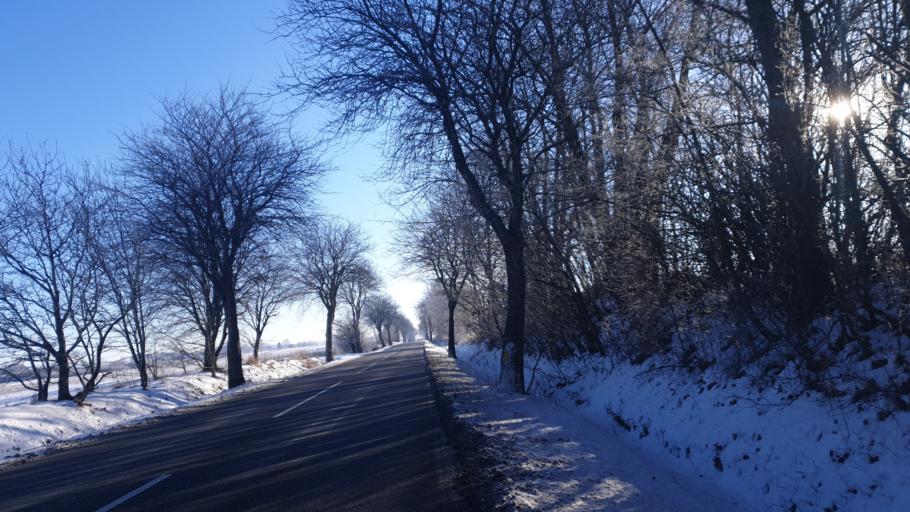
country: DK
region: Central Jutland
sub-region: Hedensted Kommune
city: Hedensted
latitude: 55.7984
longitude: 9.7358
